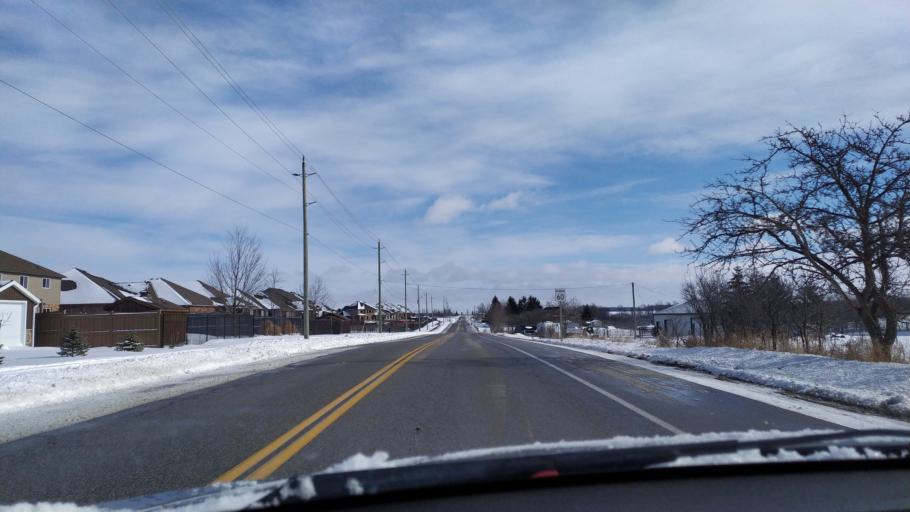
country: CA
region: Ontario
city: Stratford
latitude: 43.4704
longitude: -80.7602
